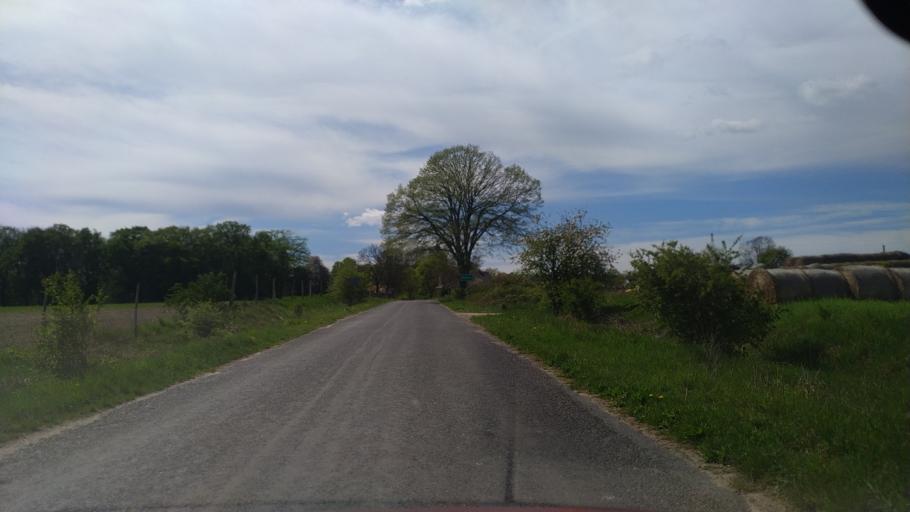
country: PL
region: West Pomeranian Voivodeship
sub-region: Powiat walecki
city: Walcz
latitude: 53.3542
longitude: 16.2929
